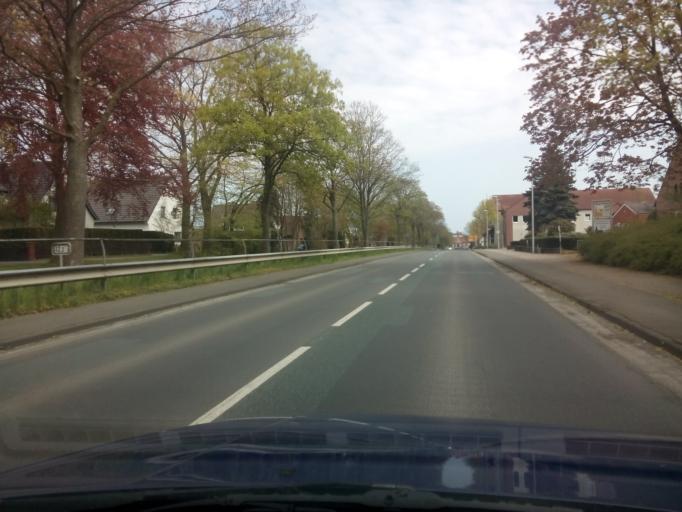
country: DE
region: Lower Saxony
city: Bruchhausen-Vilsen
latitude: 52.8279
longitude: 8.9845
